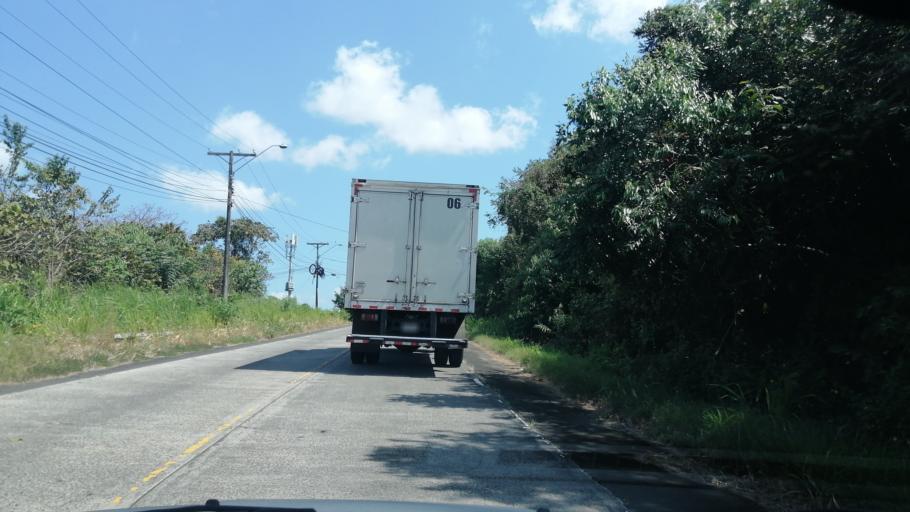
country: PA
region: Panama
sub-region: Distrito de Panama
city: Ancon
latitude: 8.9398
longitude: -79.5741
